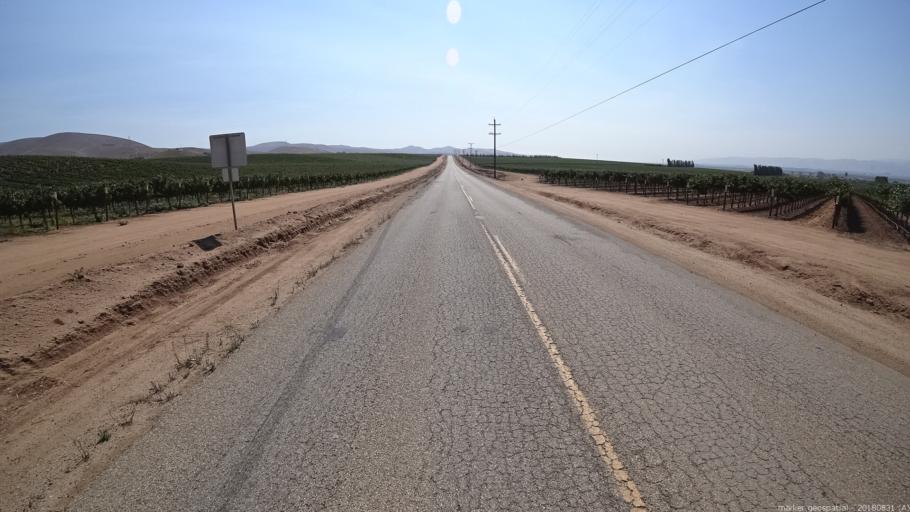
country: US
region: California
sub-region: Monterey County
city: Soledad
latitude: 36.4149
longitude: -121.2762
